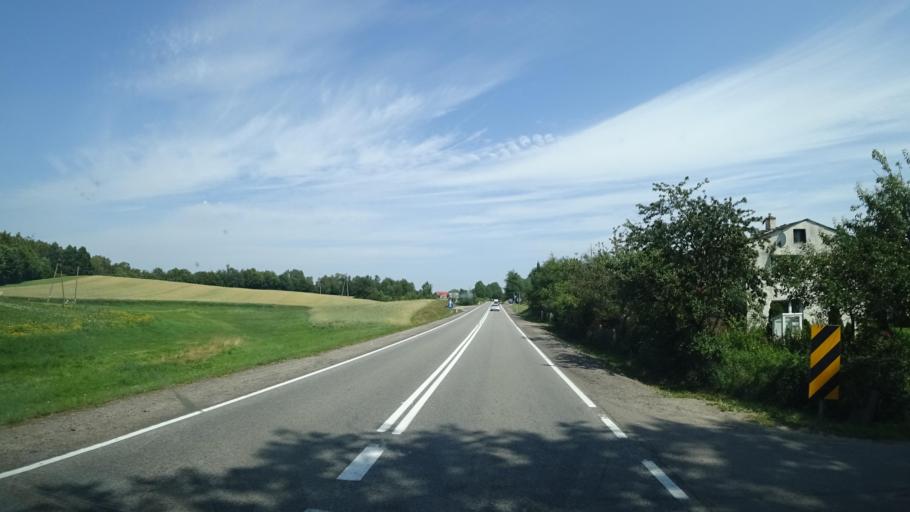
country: PL
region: Pomeranian Voivodeship
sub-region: Powiat koscierski
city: Grabowo Koscierskie
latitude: 54.2210
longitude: 18.1384
